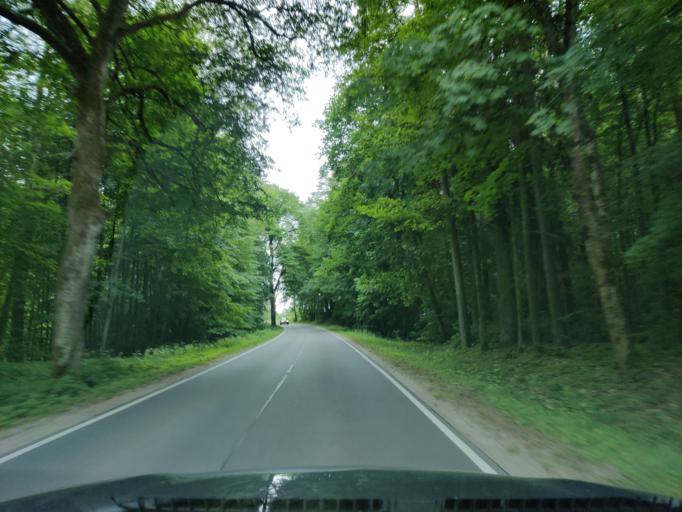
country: PL
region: Warmian-Masurian Voivodeship
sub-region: Powiat gizycki
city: Ryn
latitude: 53.8830
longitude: 21.5791
